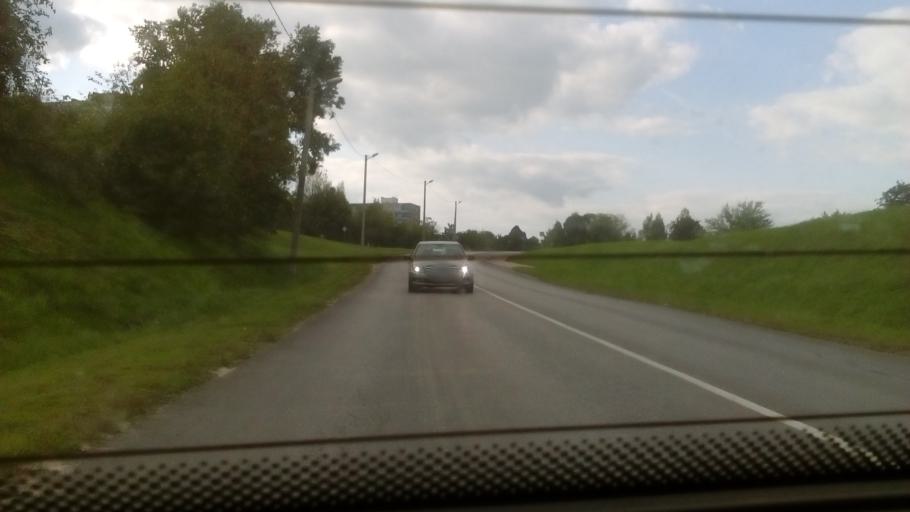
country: LT
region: Alytaus apskritis
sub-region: Alytus
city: Alytus
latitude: 54.4091
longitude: 24.0278
